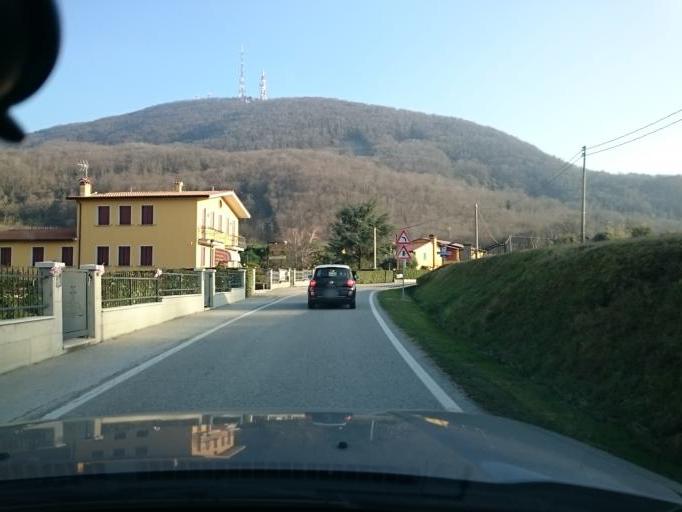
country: IT
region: Veneto
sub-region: Provincia di Padova
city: Fontanafredda
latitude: 45.3196
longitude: 11.6751
